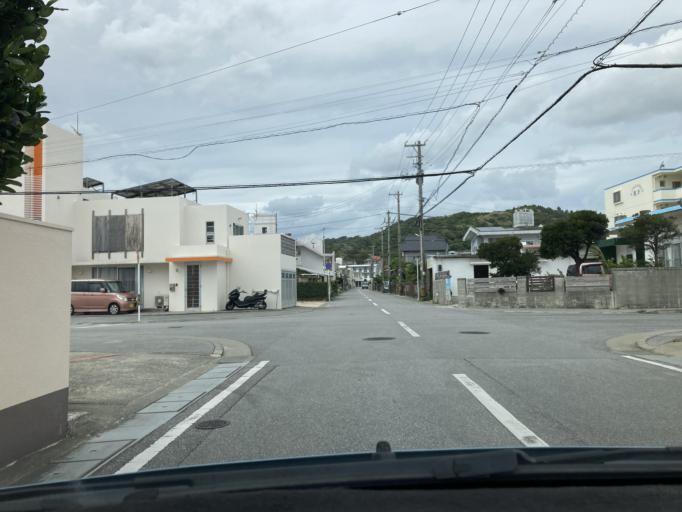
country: JP
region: Okinawa
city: Ginowan
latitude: 26.1839
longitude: 127.7773
